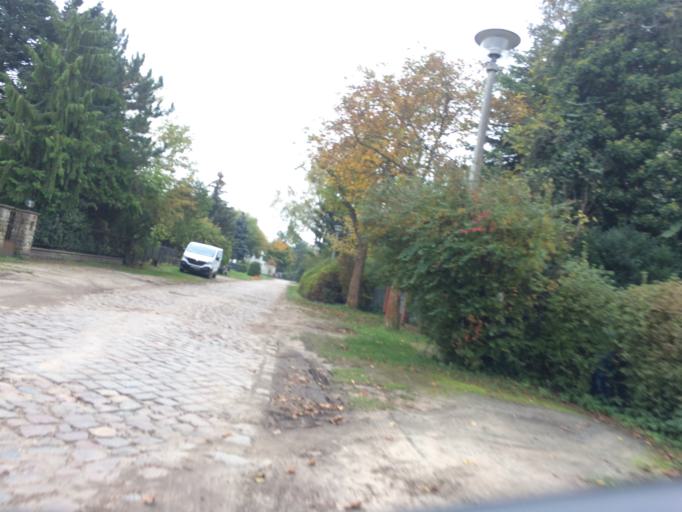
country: DE
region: Berlin
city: Buchholz
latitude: 52.5971
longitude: 13.4411
